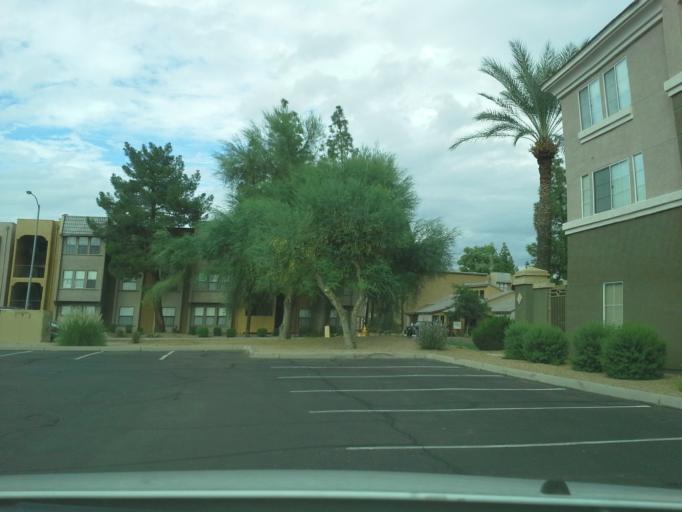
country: US
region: Arizona
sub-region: Maricopa County
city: Paradise Valley
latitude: 33.5959
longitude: -111.9841
